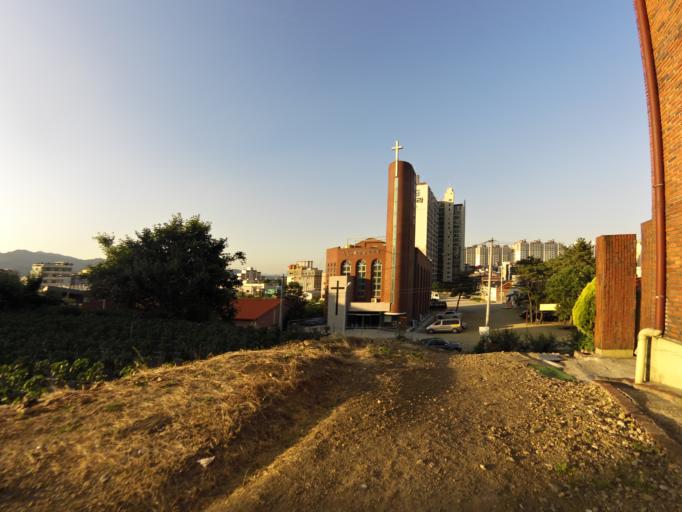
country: KR
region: Gyeongsangbuk-do
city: Gyeongsan-si
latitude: 35.8395
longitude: 128.7599
